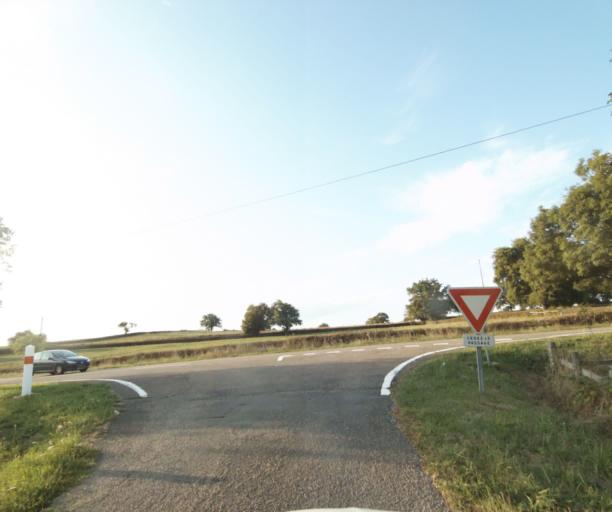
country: FR
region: Bourgogne
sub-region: Departement de Saone-et-Loire
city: Charolles
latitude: 46.4494
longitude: 4.3575
